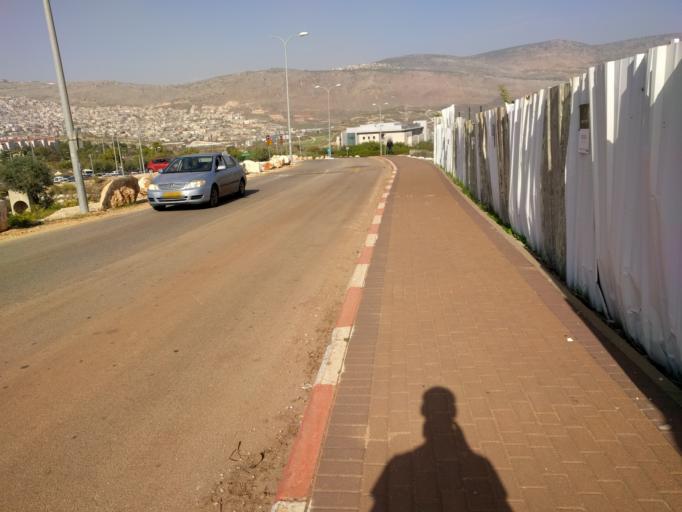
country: IL
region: Northern District
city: Karmi'el
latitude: 32.9119
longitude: 35.2805
